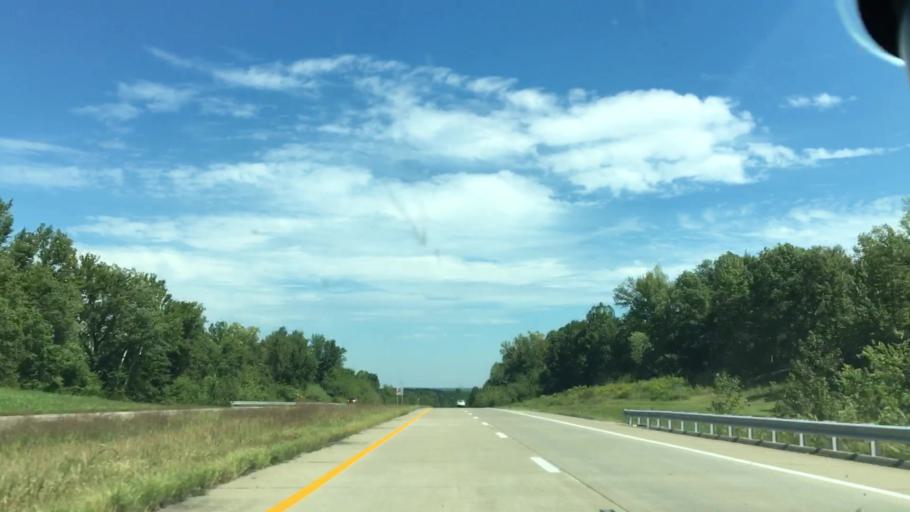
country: US
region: Indiana
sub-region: Warrick County
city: Newburgh
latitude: 37.7604
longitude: -87.3257
